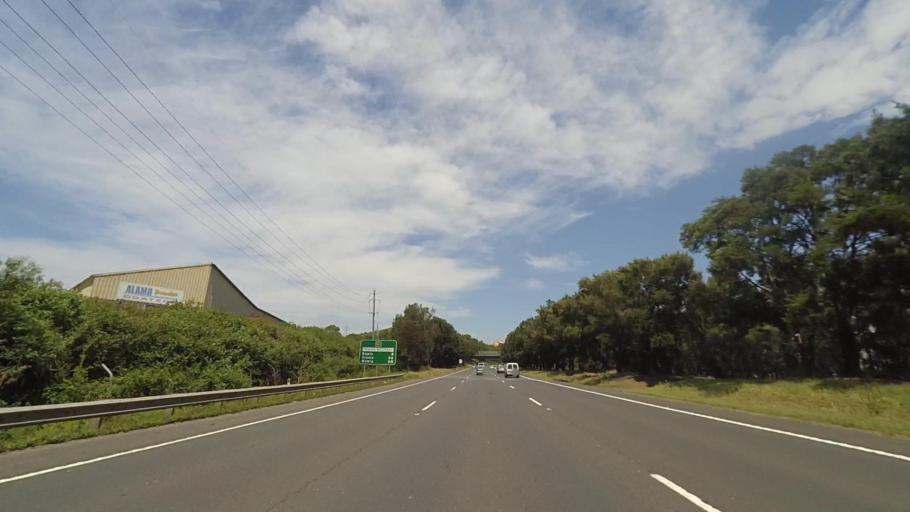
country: AU
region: New South Wales
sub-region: Wollongong
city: Berkeley
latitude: -34.4600
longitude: 150.8540
